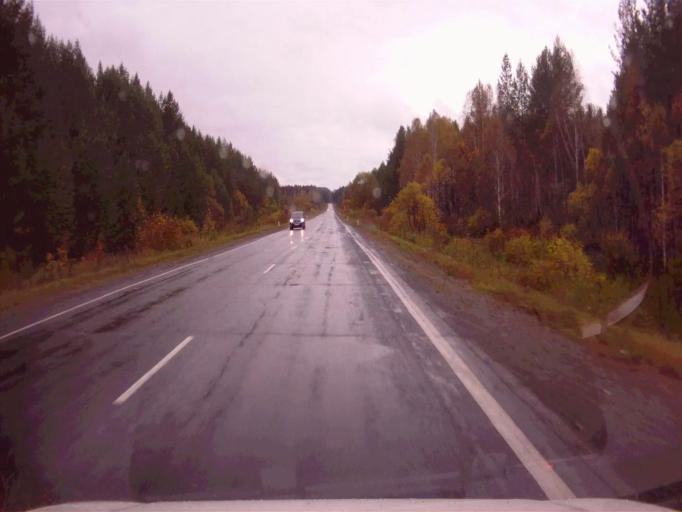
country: RU
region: Chelyabinsk
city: Verkhniy Ufaley
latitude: 56.0143
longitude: 60.3119
